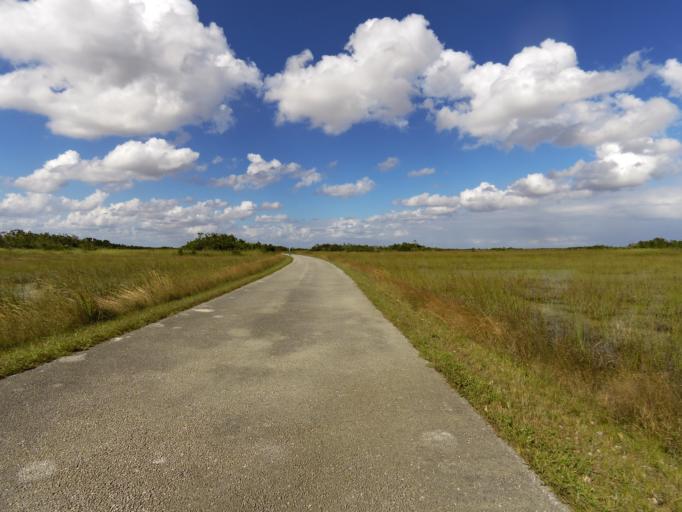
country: US
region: Florida
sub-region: Miami-Dade County
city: The Hammocks
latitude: 25.7092
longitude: -80.7613
